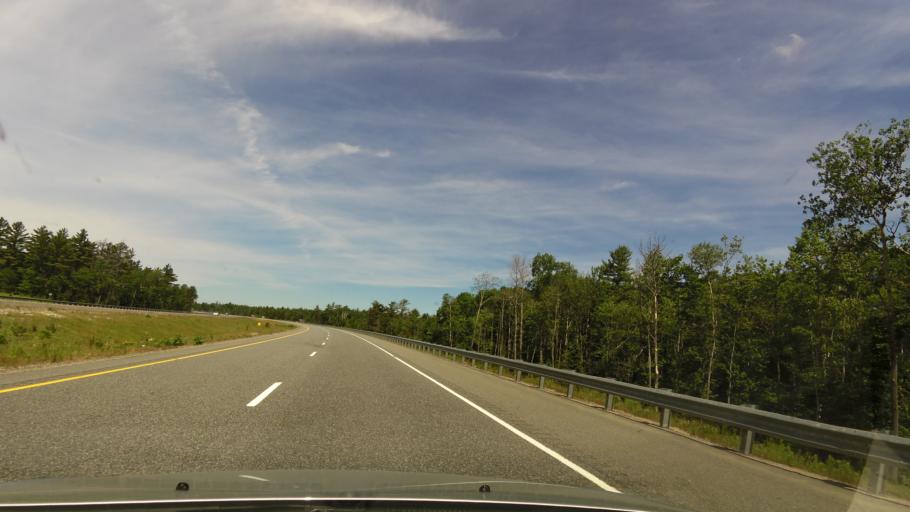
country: CA
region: Ontario
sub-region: Parry Sound District
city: Parry Sound
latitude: 45.4319
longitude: -80.0875
